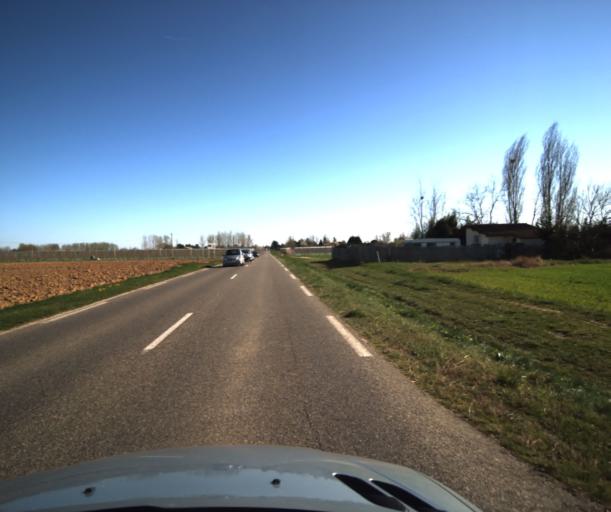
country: FR
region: Midi-Pyrenees
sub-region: Departement du Tarn-et-Garonne
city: Corbarieu
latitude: 43.9419
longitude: 1.3553
